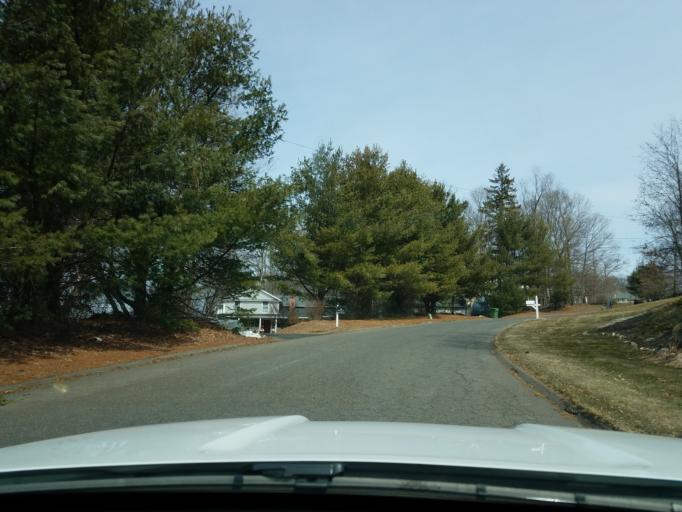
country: US
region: Connecticut
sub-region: Hartford County
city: Collinsville
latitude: 41.8030
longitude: -72.9139
